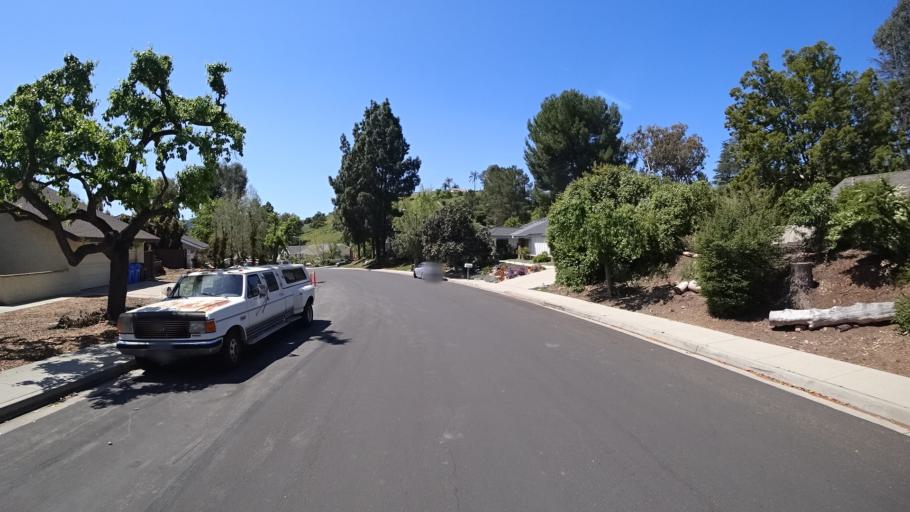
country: US
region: California
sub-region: Ventura County
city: Casa Conejo
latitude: 34.2013
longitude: -118.8916
